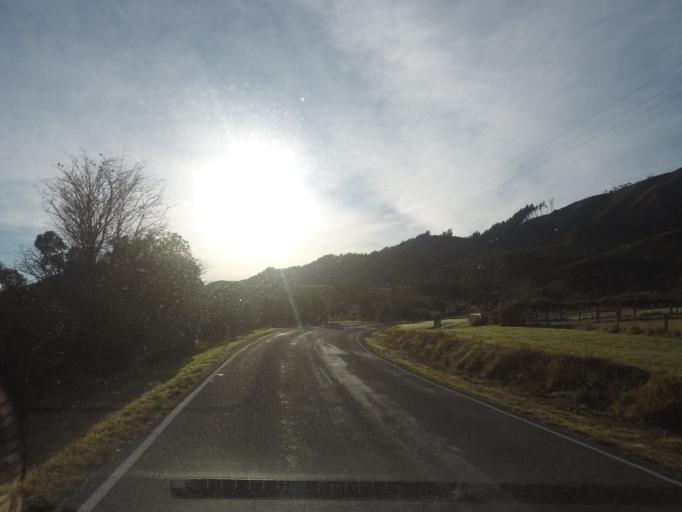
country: NZ
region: Tasman
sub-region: Tasman District
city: Takaka
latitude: -40.8192
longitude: 172.9125
